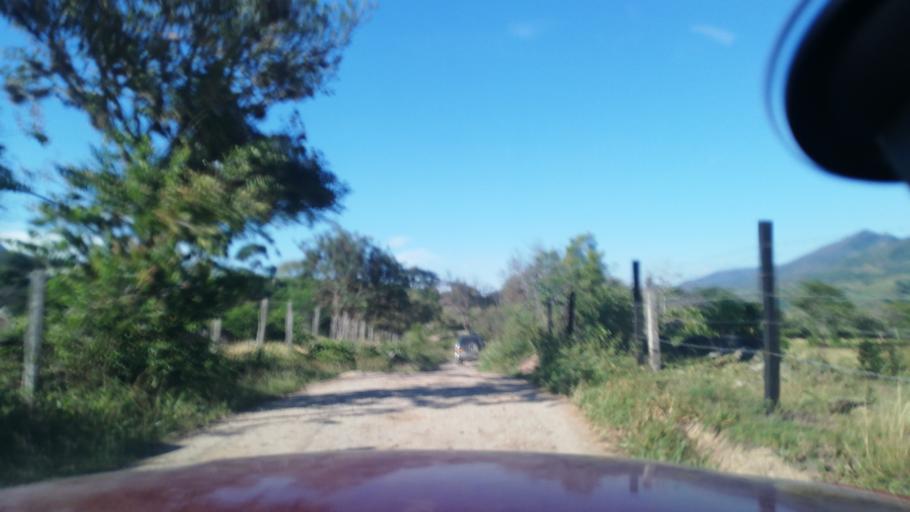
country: CO
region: Cundinamarca
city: Viani
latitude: 4.8179
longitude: -74.6166
